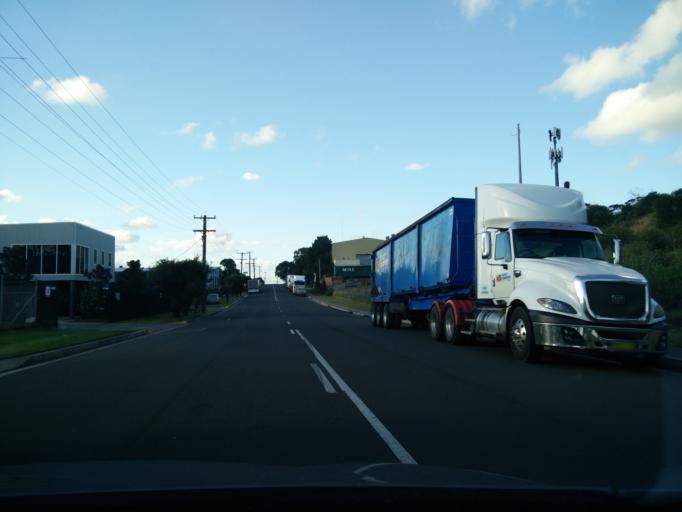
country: AU
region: New South Wales
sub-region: Wollongong
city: Cordeaux Heights
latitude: -34.4611
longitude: 150.8441
